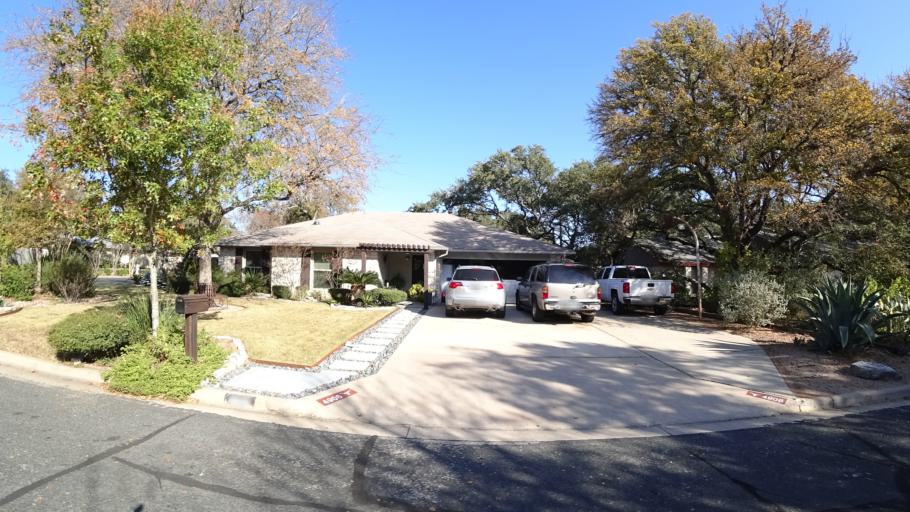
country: US
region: Texas
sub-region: Travis County
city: Barton Creek
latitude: 30.2266
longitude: -97.8459
